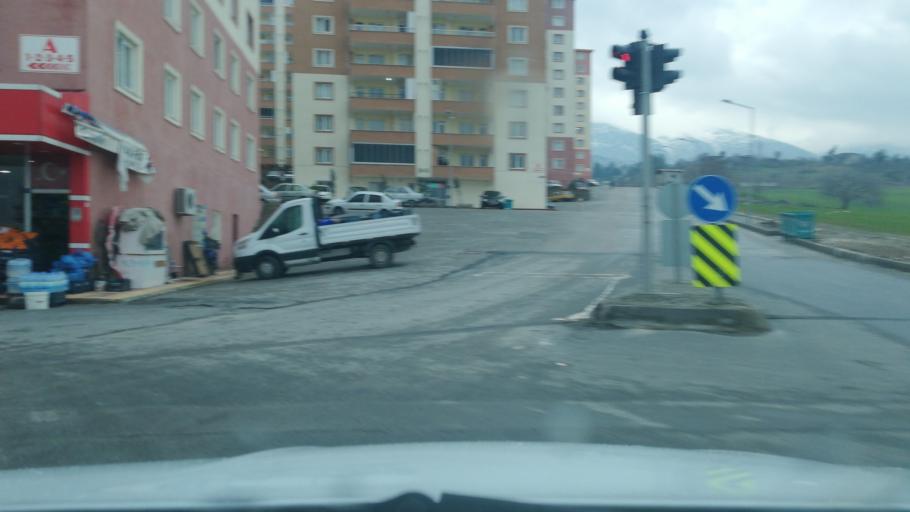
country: TR
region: Kahramanmaras
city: Kahramanmaras
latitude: 37.5795
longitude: 37.0000
